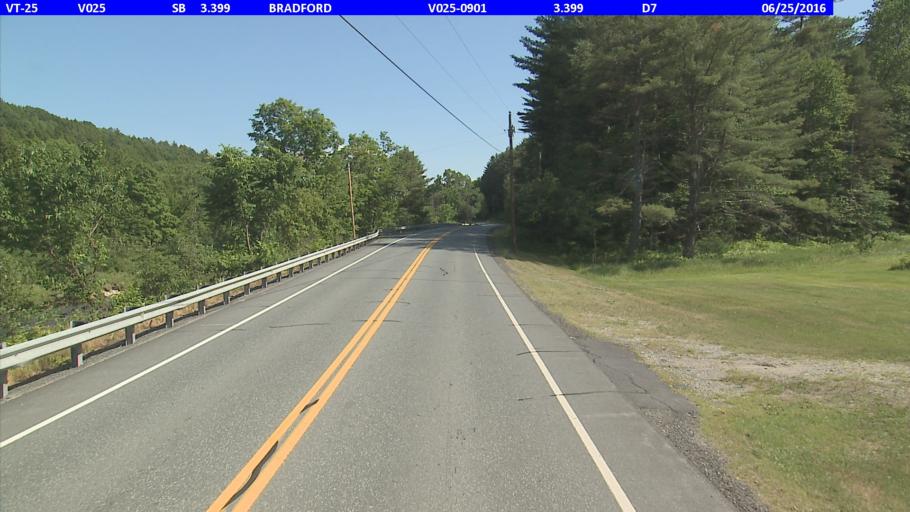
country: US
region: New Hampshire
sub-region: Grafton County
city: Orford
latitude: 44.0035
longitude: -72.1627
